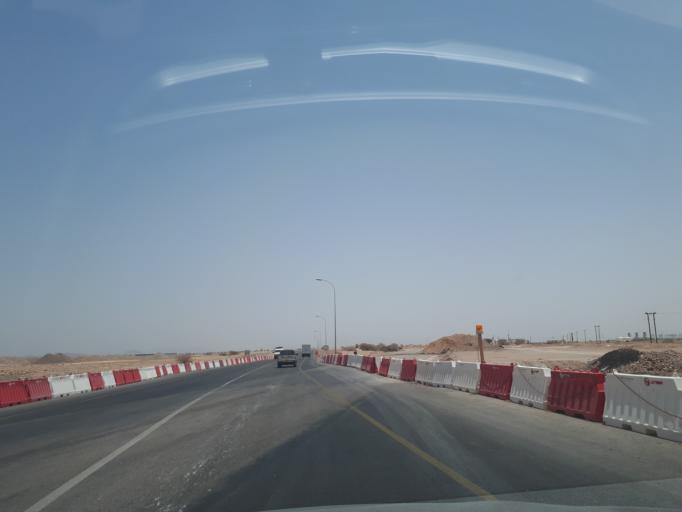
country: OM
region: Ash Sharqiyah
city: Badiyah
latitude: 22.4066
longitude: 59.0614
